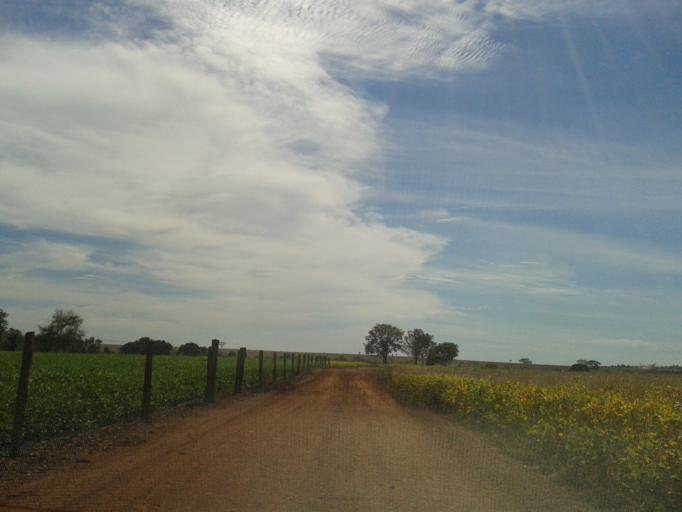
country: BR
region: Minas Gerais
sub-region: Capinopolis
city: Capinopolis
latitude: -18.6525
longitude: -49.7049
